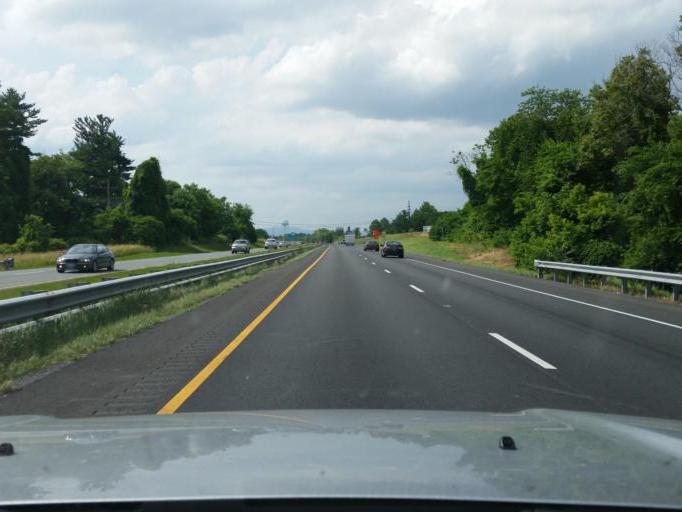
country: US
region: Maryland
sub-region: Frederick County
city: Ballenger Creek
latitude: 39.3738
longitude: -77.4048
